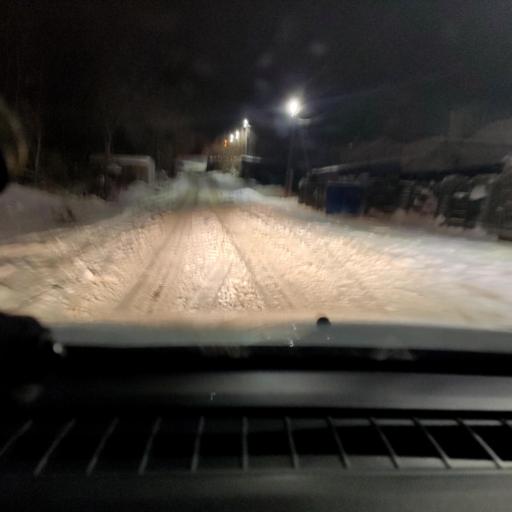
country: RU
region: Samara
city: Samara
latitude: 53.1737
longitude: 50.1665
